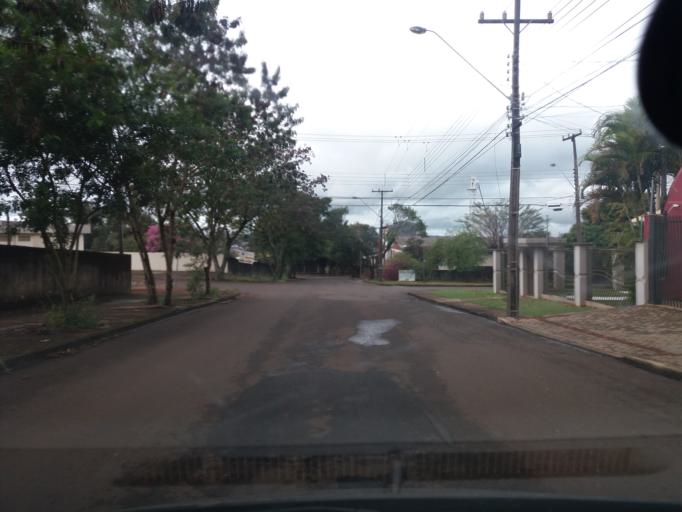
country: BR
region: Parana
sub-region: Cascavel
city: Cascavel
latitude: -24.9781
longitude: -53.4505
